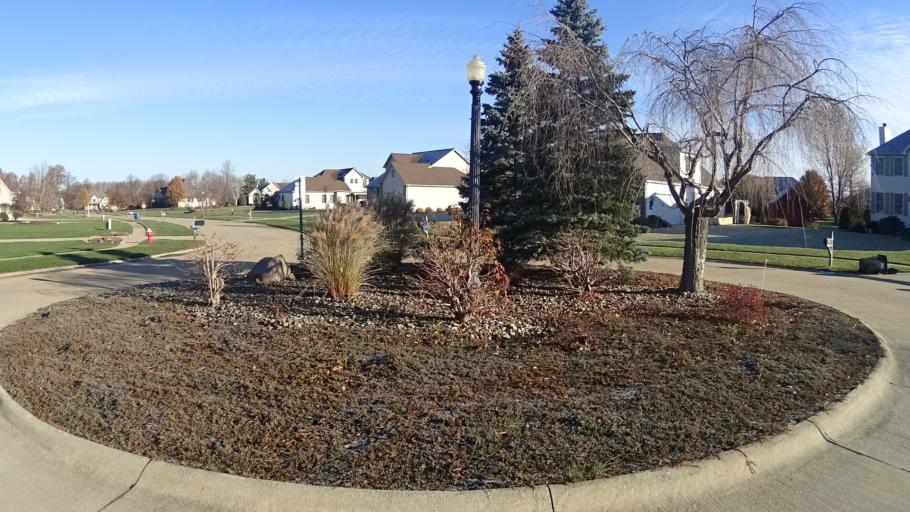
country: US
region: Ohio
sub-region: Lorain County
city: Sheffield
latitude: 41.4294
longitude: -82.0731
